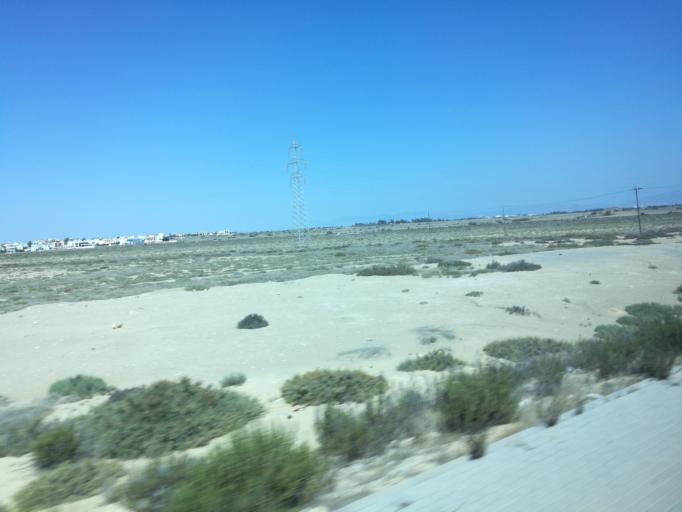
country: CY
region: Ammochostos
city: Famagusta
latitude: 35.1663
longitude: 33.8991
